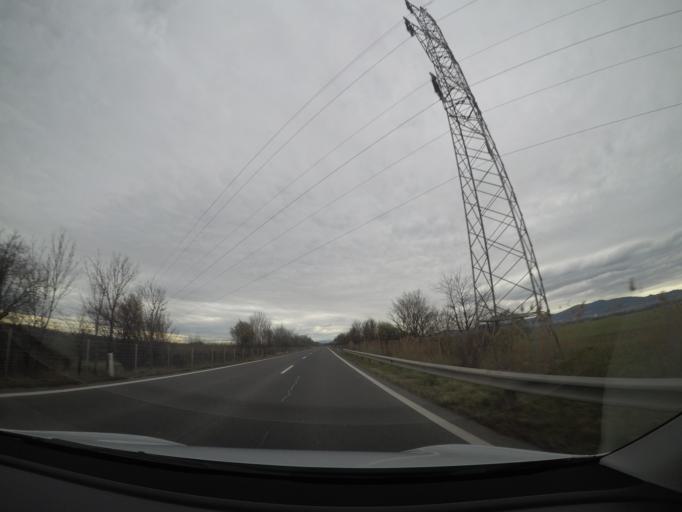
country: AT
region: Lower Austria
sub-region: Politischer Bezirk Modling
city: Munchendorf
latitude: 48.0408
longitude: 16.3723
